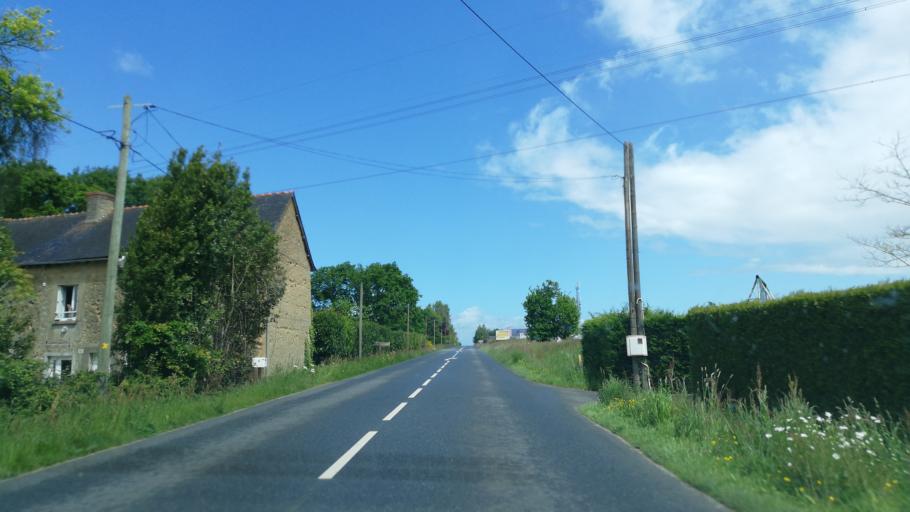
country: FR
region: Brittany
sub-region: Departement d'Ille-et-Vilaine
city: Irodouer
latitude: 48.2399
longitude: -1.9480
